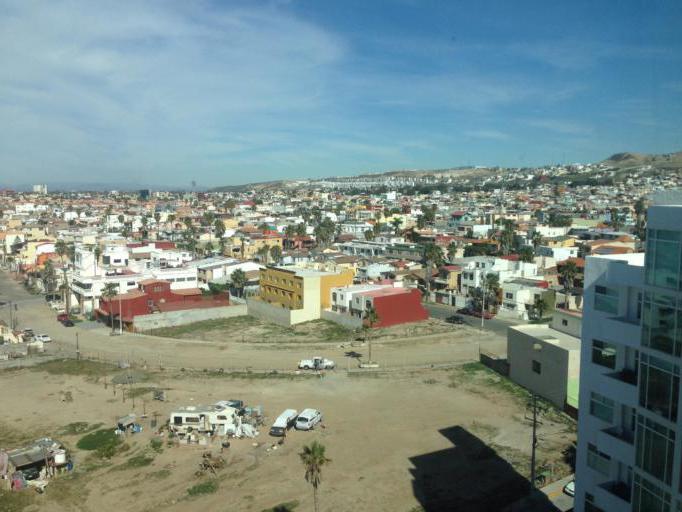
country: MX
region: Baja California
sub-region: Tijuana
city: La Esperanza [Granjas Familiares]
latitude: 32.5077
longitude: -117.1233
